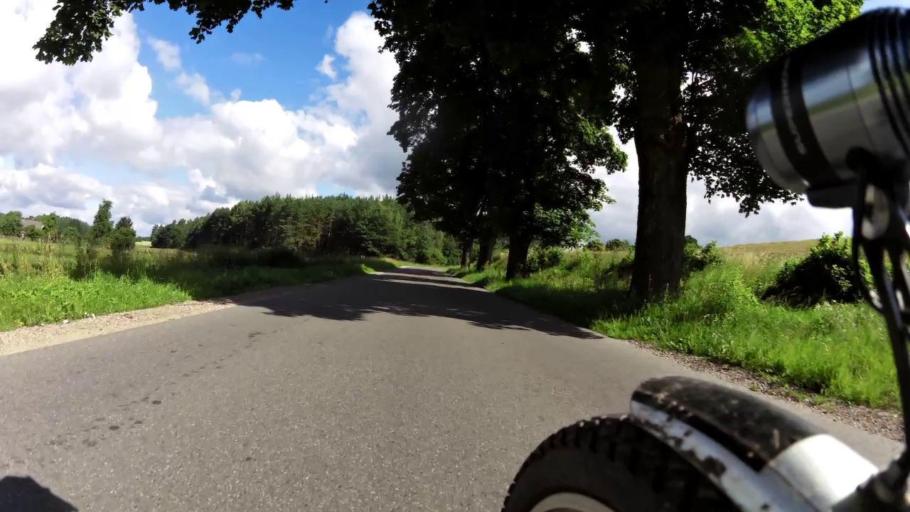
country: PL
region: West Pomeranian Voivodeship
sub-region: Powiat swidwinski
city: Rabino
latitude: 53.7812
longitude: 15.8978
